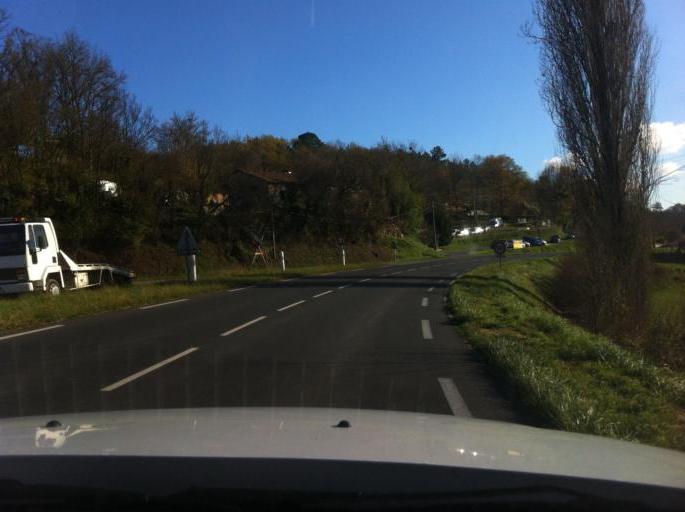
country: FR
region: Aquitaine
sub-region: Departement de la Dordogne
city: Rouffignac-Saint-Cernin-de-Reilhac
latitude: 45.0433
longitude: 0.8876
